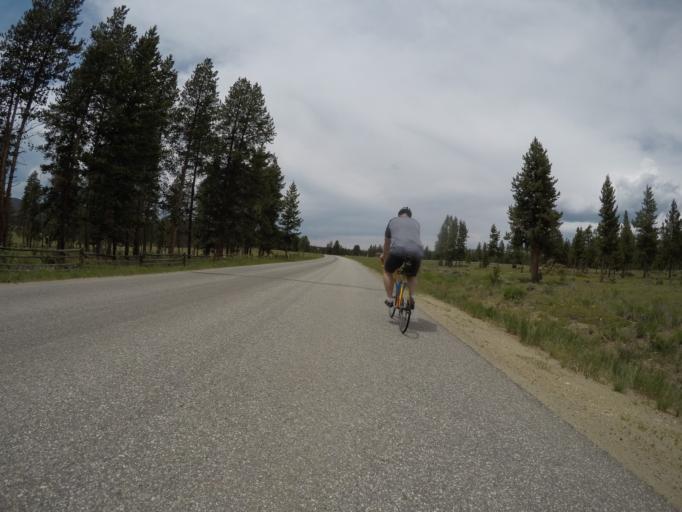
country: US
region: Colorado
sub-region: Grand County
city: Fraser
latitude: 39.9862
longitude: -105.8792
